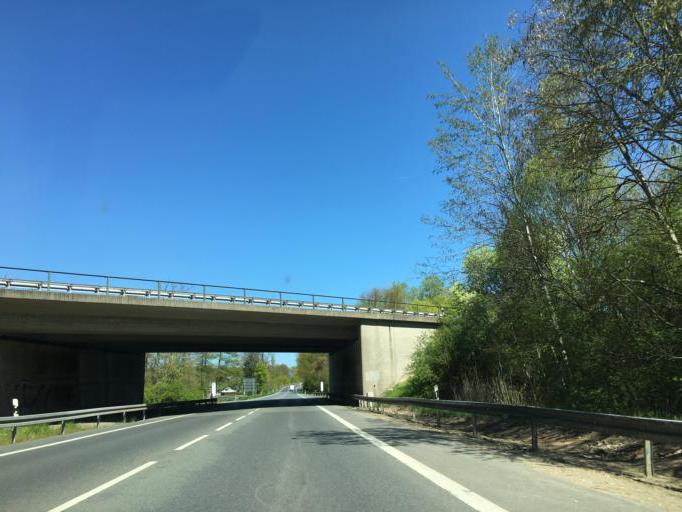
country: DE
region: Hesse
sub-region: Regierungsbezirk Darmstadt
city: Neu Isenburg
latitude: 50.0493
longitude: 8.7190
